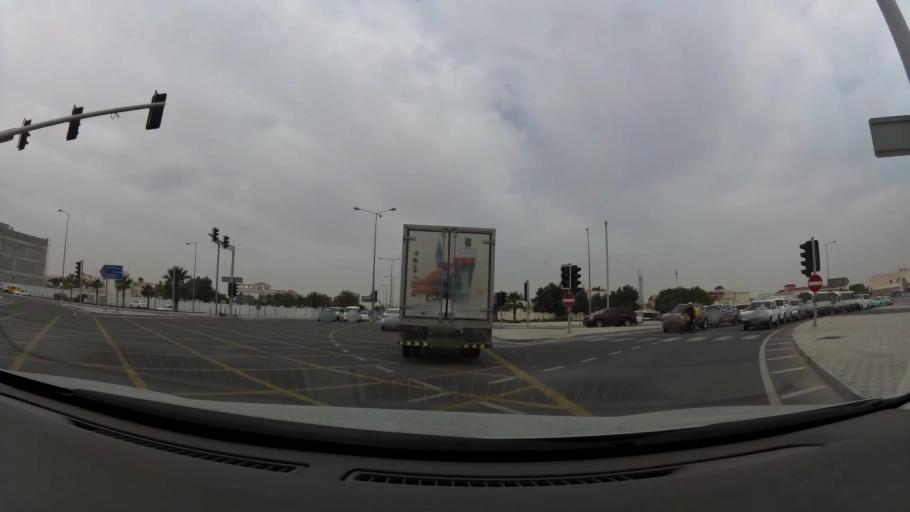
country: QA
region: Baladiyat ar Rayyan
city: Ar Rayyan
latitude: 25.2335
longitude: 51.4459
